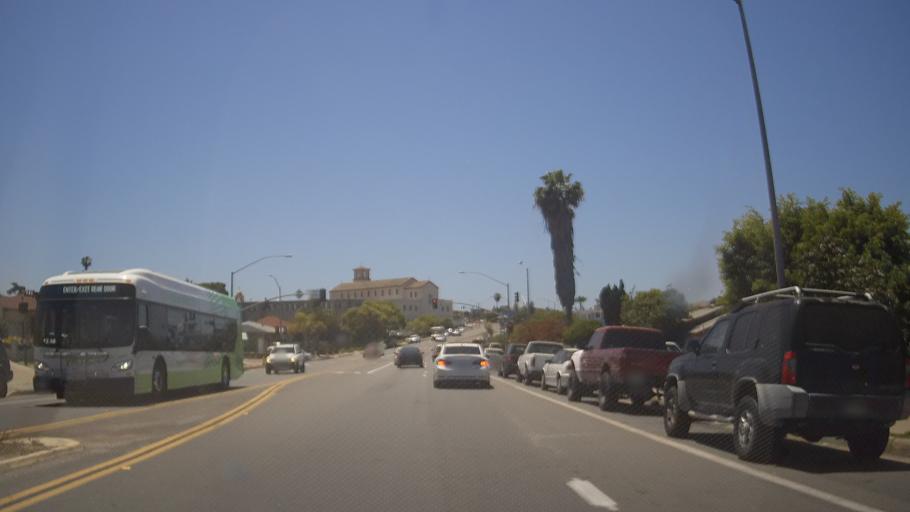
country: US
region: California
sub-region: San Diego County
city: National City
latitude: 32.7062
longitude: -117.0819
